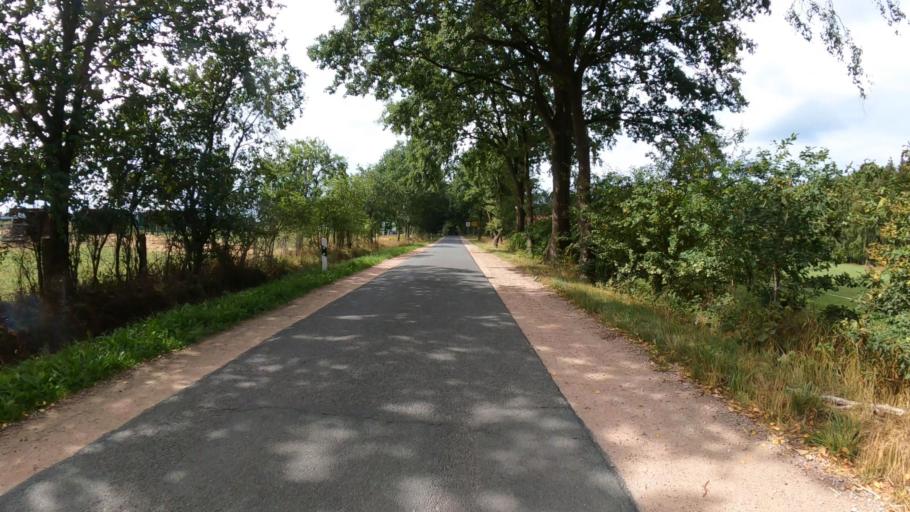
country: DE
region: Lower Saxony
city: Appel
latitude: 53.3813
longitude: 9.7614
